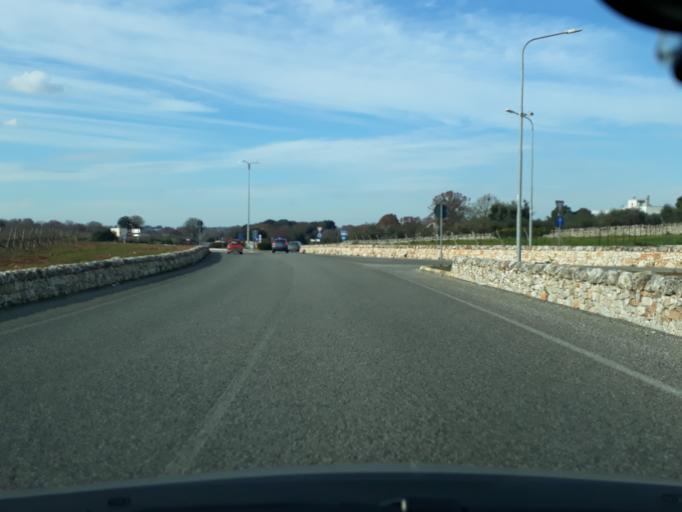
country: IT
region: Apulia
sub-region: Provincia di Bari
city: Locorotondo
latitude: 40.7576
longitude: 17.3423
